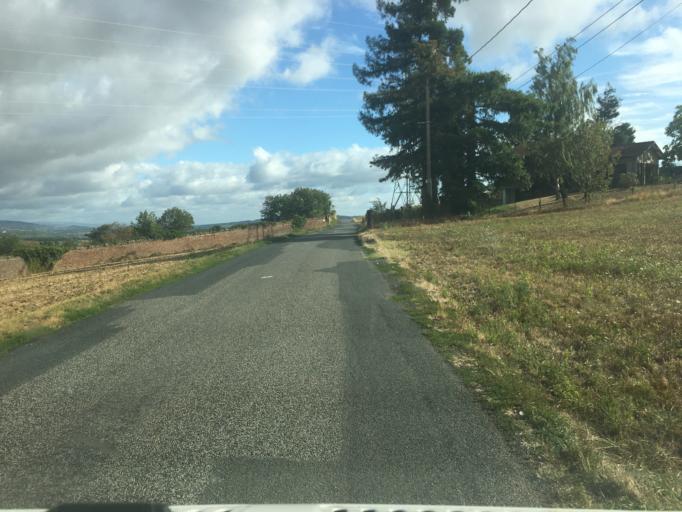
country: FR
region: Rhone-Alpes
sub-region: Departement du Rhone
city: Sourcieux-les-Mines
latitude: 45.8169
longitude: 4.6239
